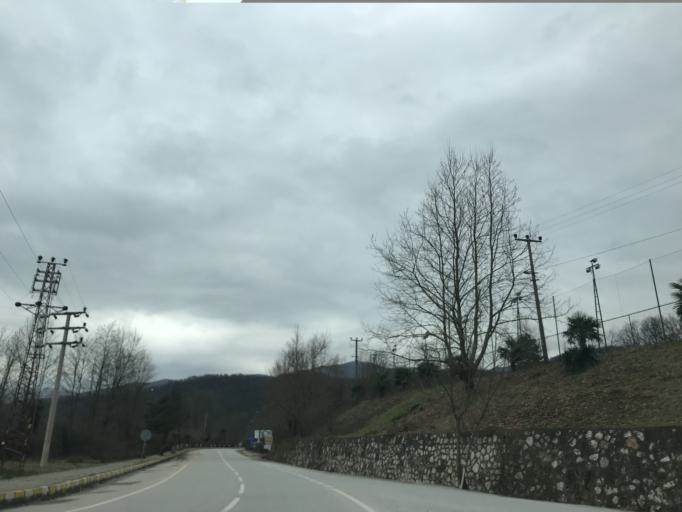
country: TR
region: Yalova
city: Termal
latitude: 40.6051
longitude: 29.1830
